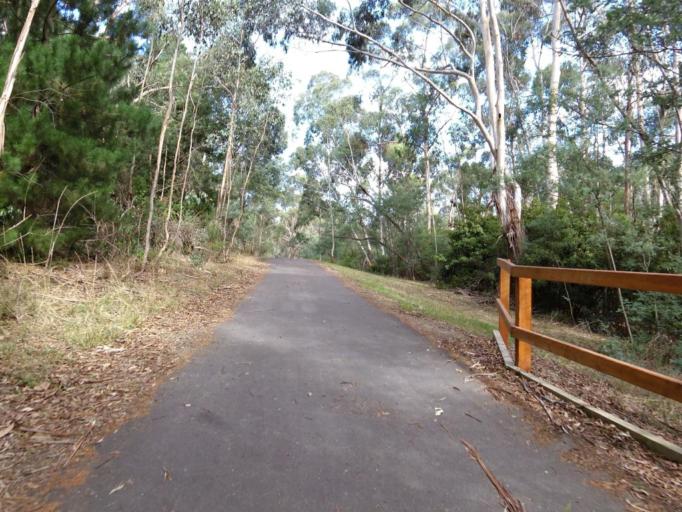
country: AU
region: Victoria
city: Mitcham
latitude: -37.8016
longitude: 145.2030
